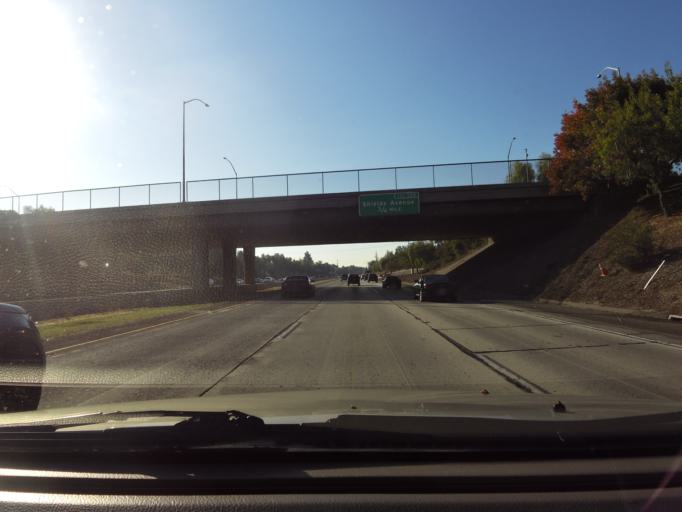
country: US
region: California
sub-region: Fresno County
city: Fresno
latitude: 36.7947
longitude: -119.7852
